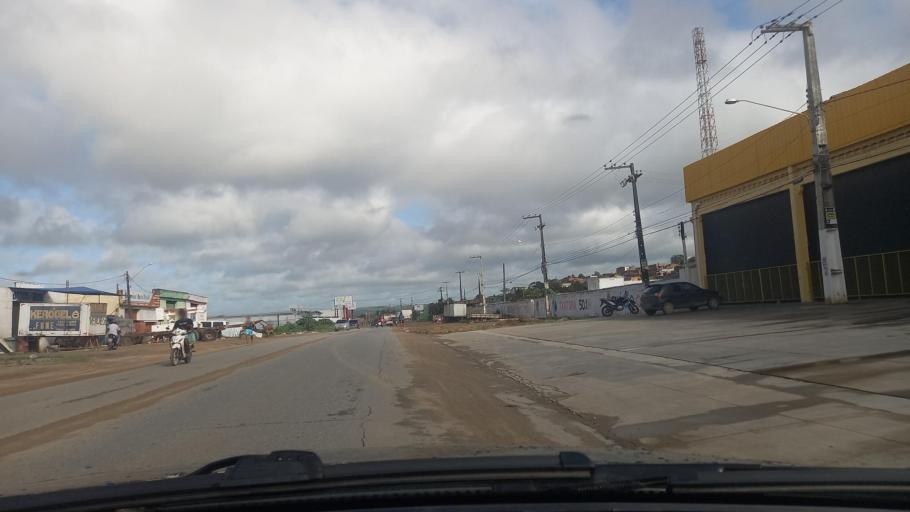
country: BR
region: Pernambuco
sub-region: Vitoria De Santo Antao
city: Vitoria de Santo Antao
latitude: -8.1172
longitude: -35.3091
